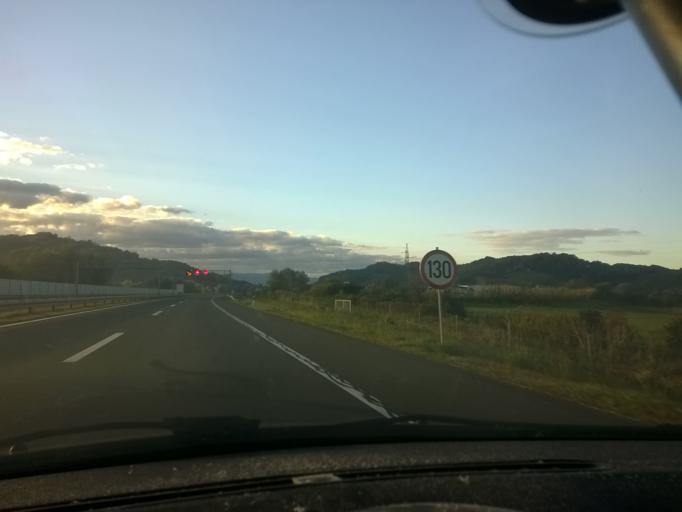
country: HR
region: Krapinsko-Zagorska
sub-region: Grad Krapina
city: Krapina
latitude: 46.1251
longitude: 15.8898
